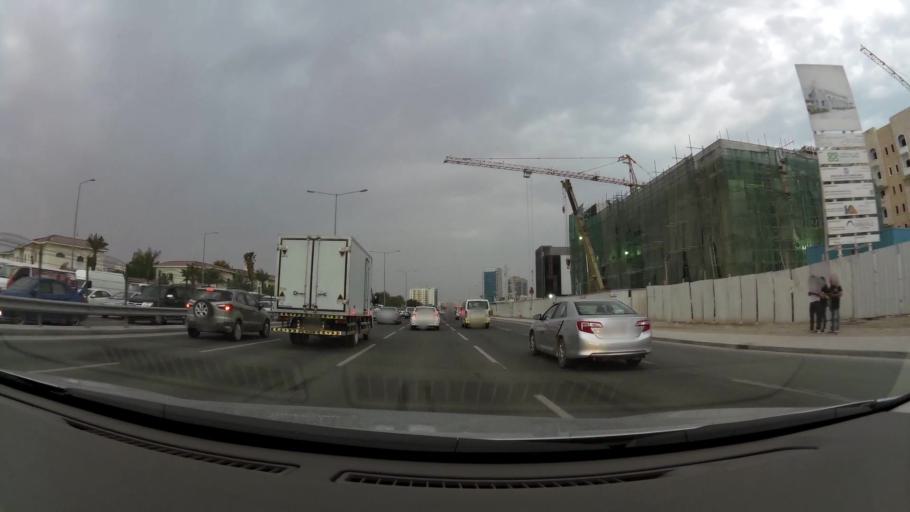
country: QA
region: Baladiyat ad Dawhah
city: Doha
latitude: 25.2687
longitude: 51.5140
